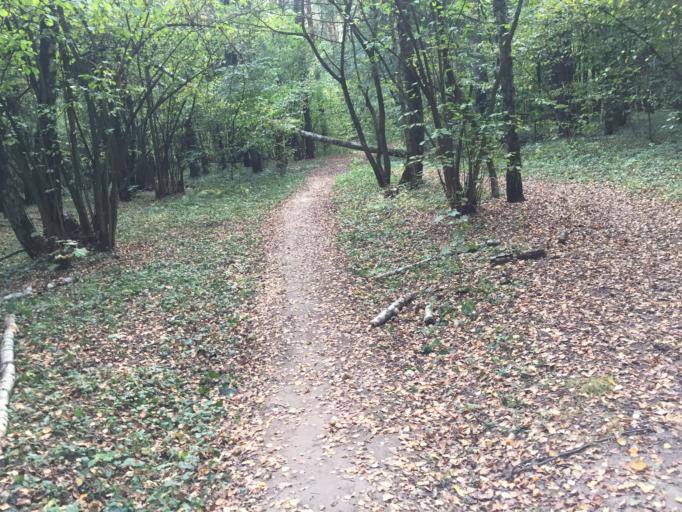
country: RU
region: Moscow
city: Babushkin
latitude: 55.8695
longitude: 37.7332
